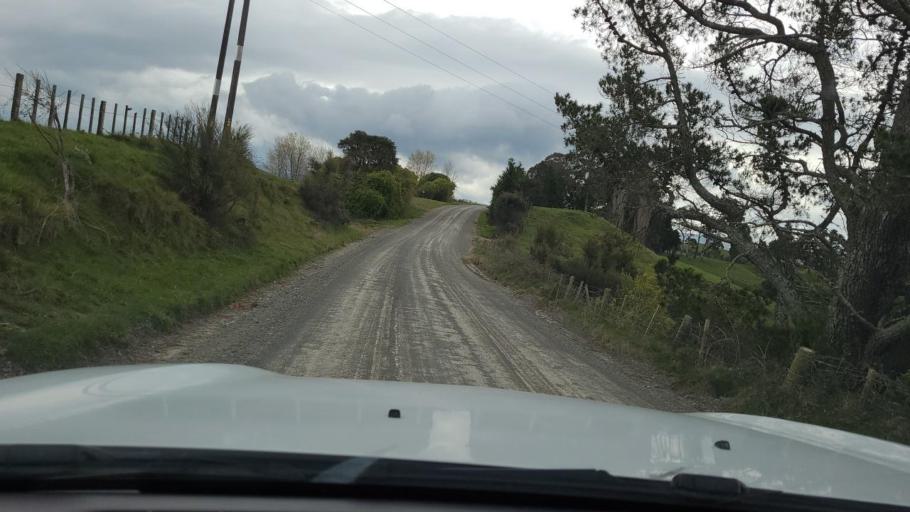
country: NZ
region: Hawke's Bay
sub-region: Napier City
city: Napier
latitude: -39.3182
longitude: 176.8392
